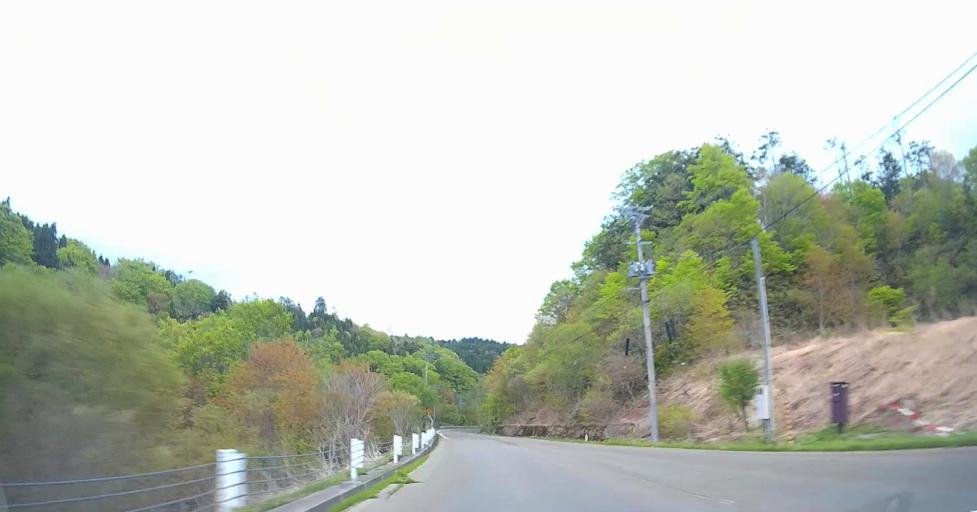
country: JP
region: Aomori
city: Goshogawara
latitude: 41.1017
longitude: 140.5490
